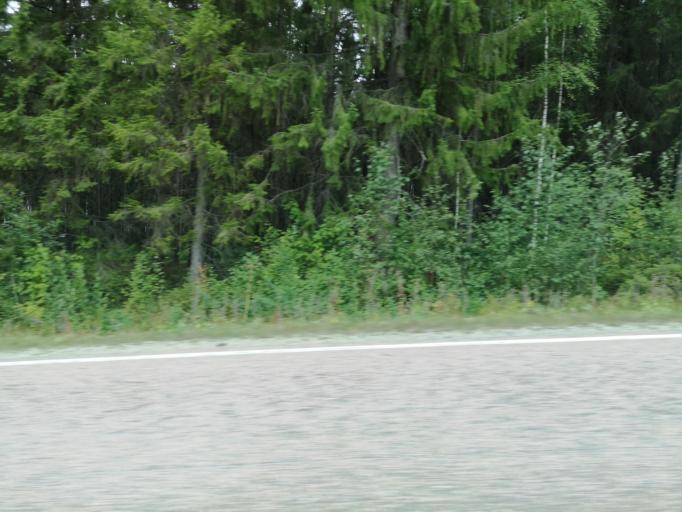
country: FI
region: Central Finland
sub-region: Jyvaeskylae
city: Hankasalmi
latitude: 62.3568
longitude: 26.4814
